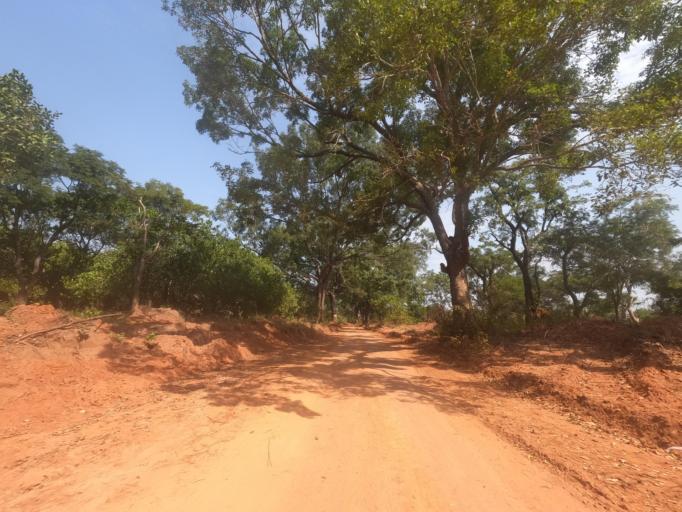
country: GW
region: Oio
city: Bissora
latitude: 12.4362
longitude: -15.5600
